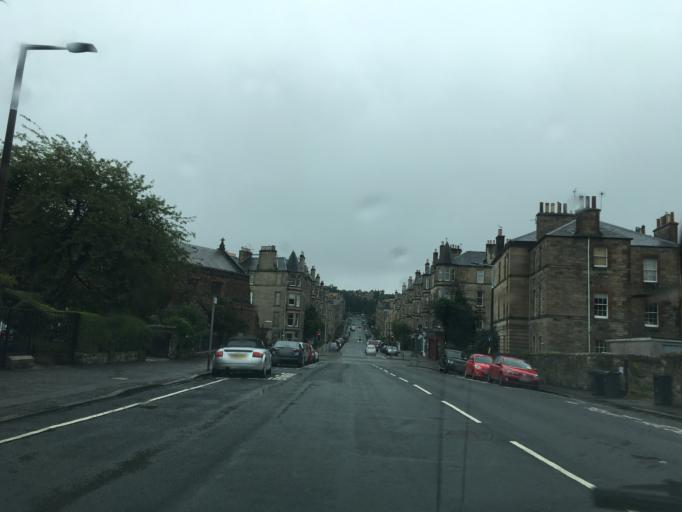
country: GB
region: Scotland
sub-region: Edinburgh
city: Edinburgh
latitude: 55.9604
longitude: -3.2191
